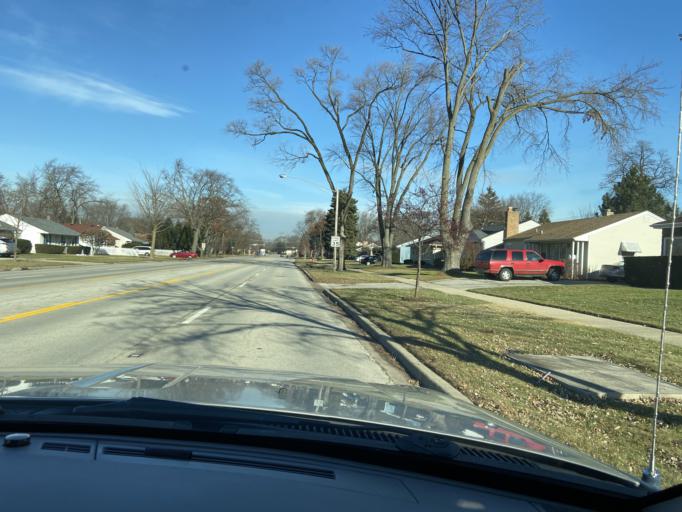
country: US
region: Illinois
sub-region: Cook County
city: Des Plaines
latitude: 42.0353
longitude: -87.9089
